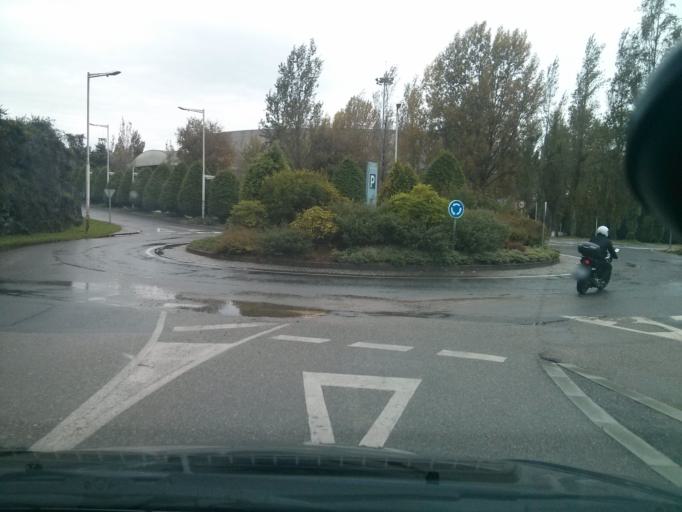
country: ES
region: Galicia
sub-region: Provincia da Coruna
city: Santiago de Compostela
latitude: 42.8766
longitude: -8.5284
